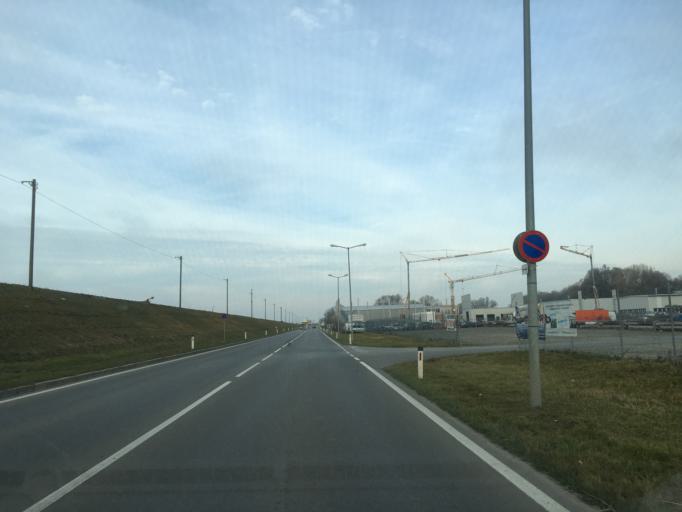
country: AT
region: Vorarlberg
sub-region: Politischer Bezirk Bregenz
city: Fussach
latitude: 47.4733
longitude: 9.6712
